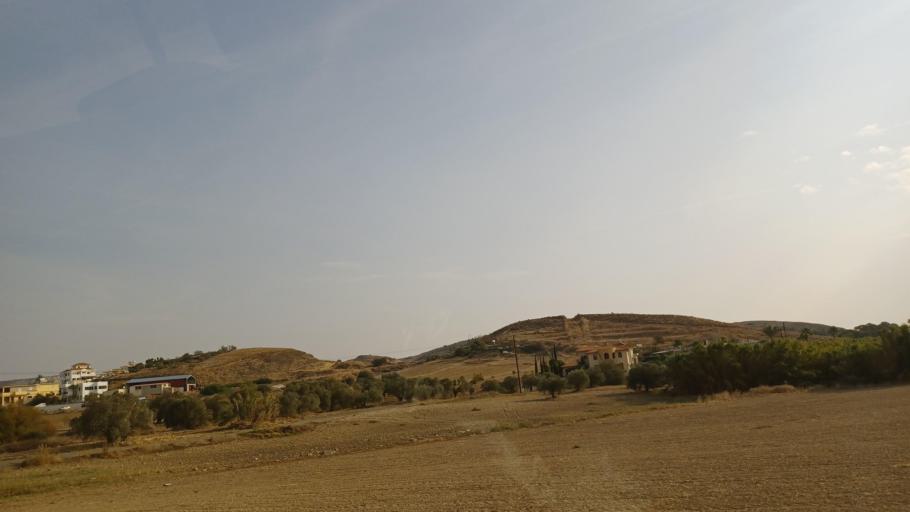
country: CY
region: Larnaka
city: Troulloi
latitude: 35.0250
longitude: 33.6119
